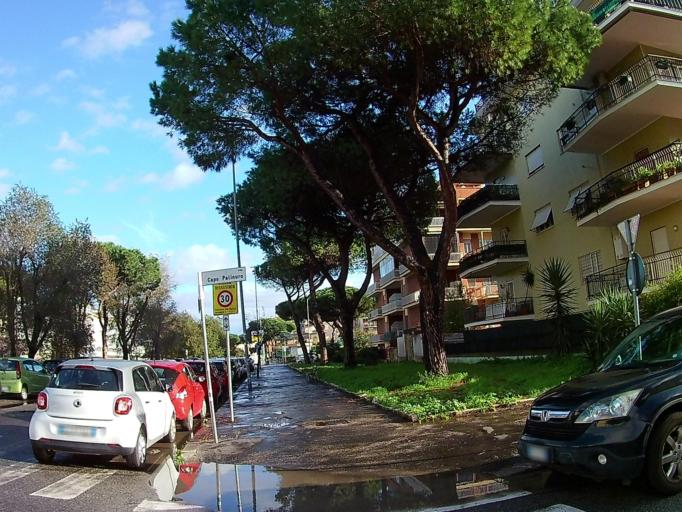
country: IT
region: Latium
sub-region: Citta metropolitana di Roma Capitale
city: Lido di Ostia
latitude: 41.7360
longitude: 12.2863
